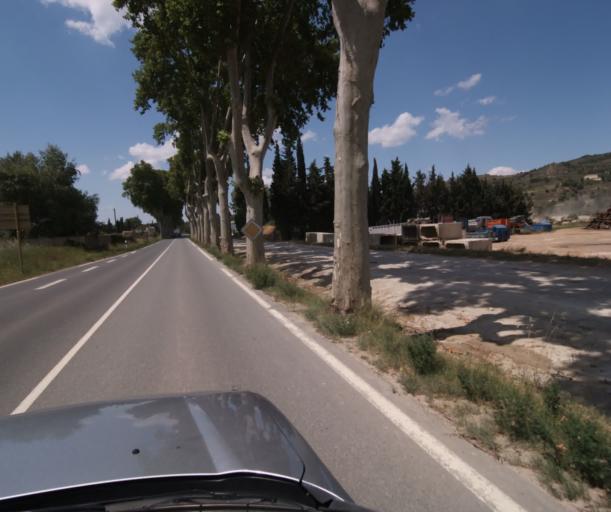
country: FR
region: Languedoc-Roussillon
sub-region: Departement de l'Aude
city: Limoux
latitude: 43.0403
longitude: 2.2419
